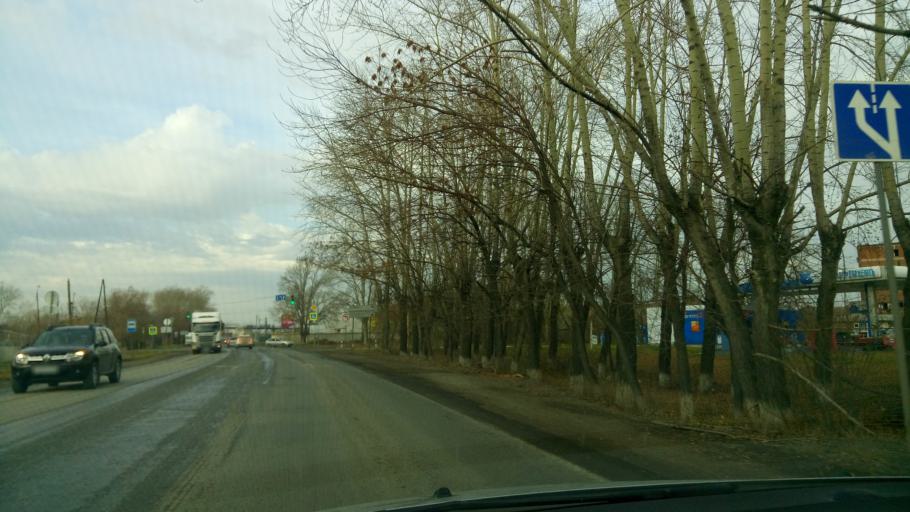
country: RU
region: Sverdlovsk
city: Bogdanovich
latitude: 56.7743
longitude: 62.0354
